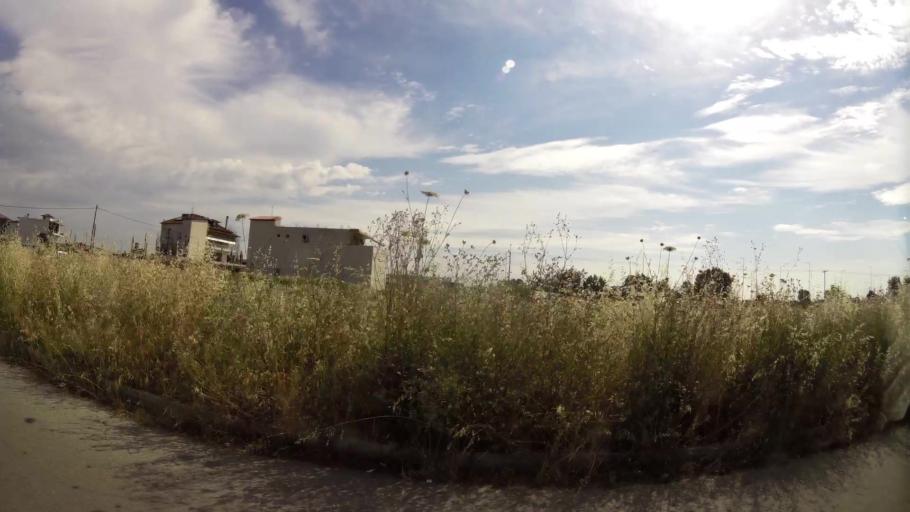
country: GR
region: Central Macedonia
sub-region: Nomos Pierias
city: Katerini
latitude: 40.2760
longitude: 22.5185
